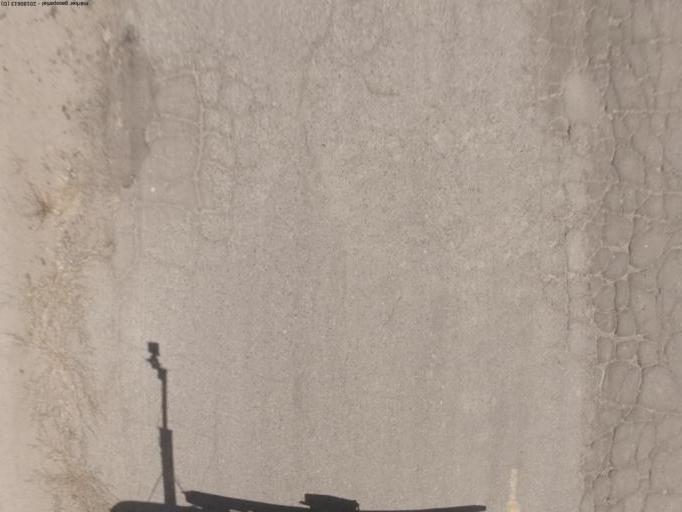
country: US
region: California
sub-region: Madera County
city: Chowchilla
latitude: 37.0349
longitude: -120.4013
